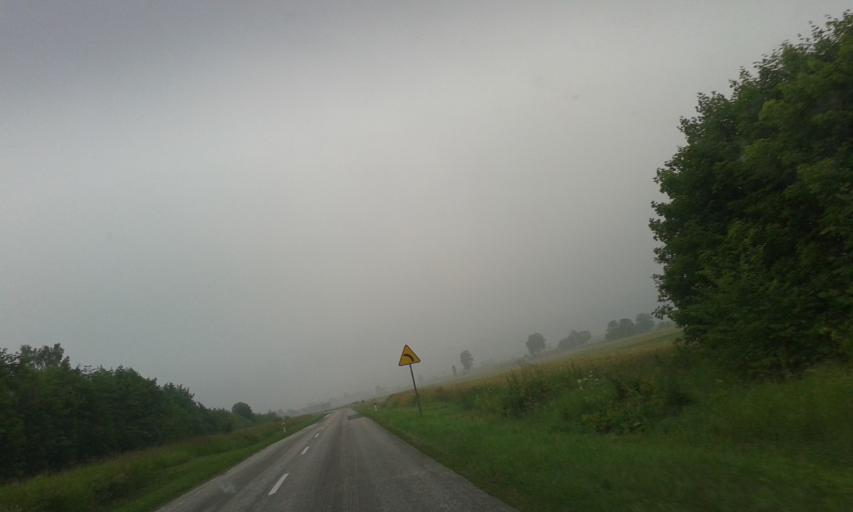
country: PL
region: Pomeranian Voivodeship
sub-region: Powiat czluchowski
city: Debrzno
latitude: 53.5209
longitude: 17.2327
